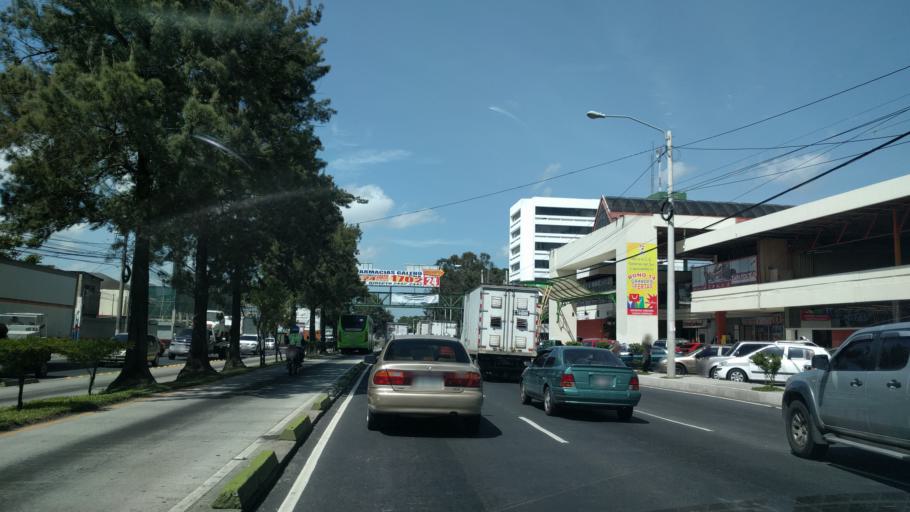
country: GT
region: Guatemala
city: Mixco
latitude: 14.5912
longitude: -90.5600
